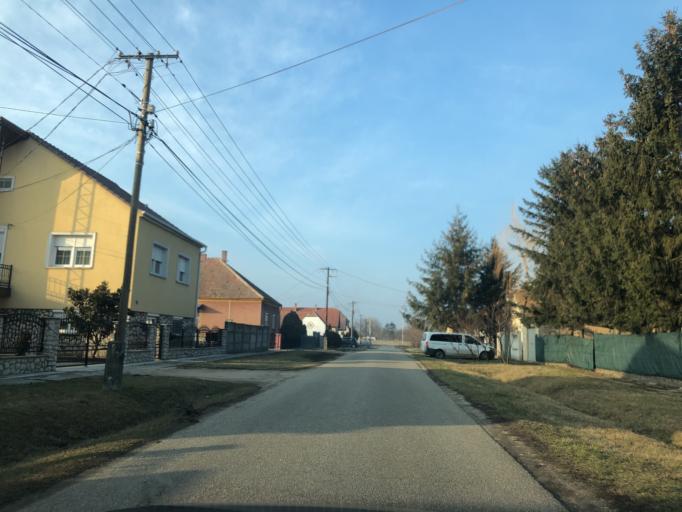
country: HU
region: Gyor-Moson-Sopron
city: Kapuvar
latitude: 47.6015
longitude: 17.0822
